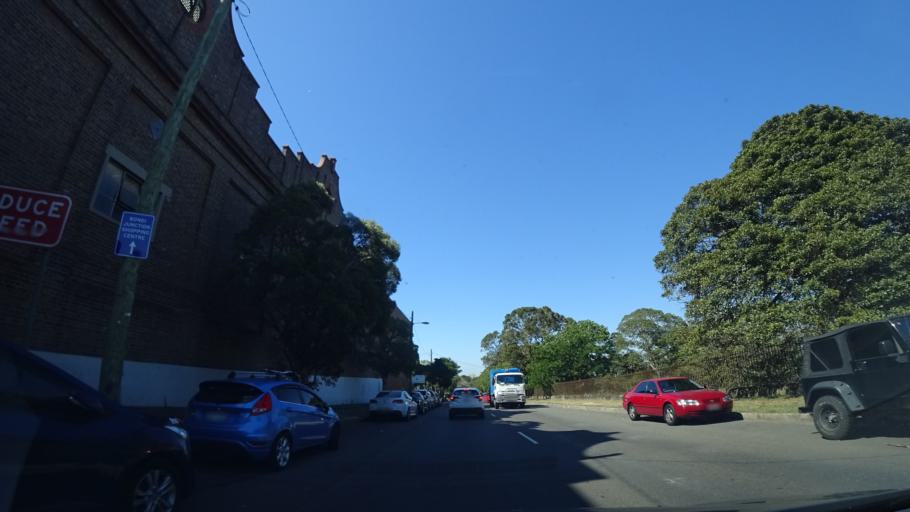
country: AU
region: New South Wales
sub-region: Waverley
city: Bondi Junction
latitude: -33.8922
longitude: 151.2415
